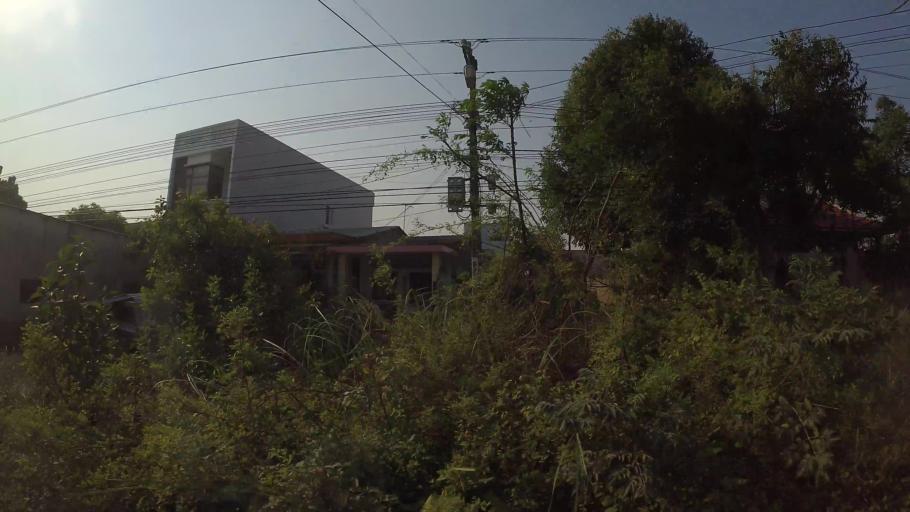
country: VN
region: Quang Nam
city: Quang Nam
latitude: 15.9438
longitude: 108.2573
